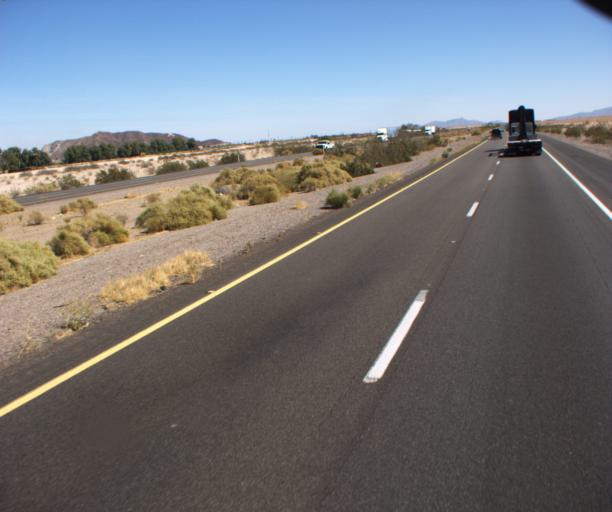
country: US
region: Arizona
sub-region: Yuma County
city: Wellton
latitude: 32.6772
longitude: -114.0420
